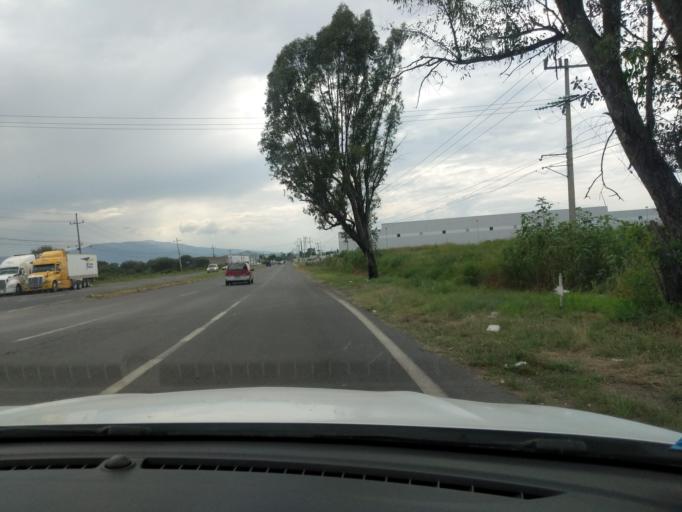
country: MX
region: Jalisco
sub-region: El Salto
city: El Muey
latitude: 20.5012
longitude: -103.2238
